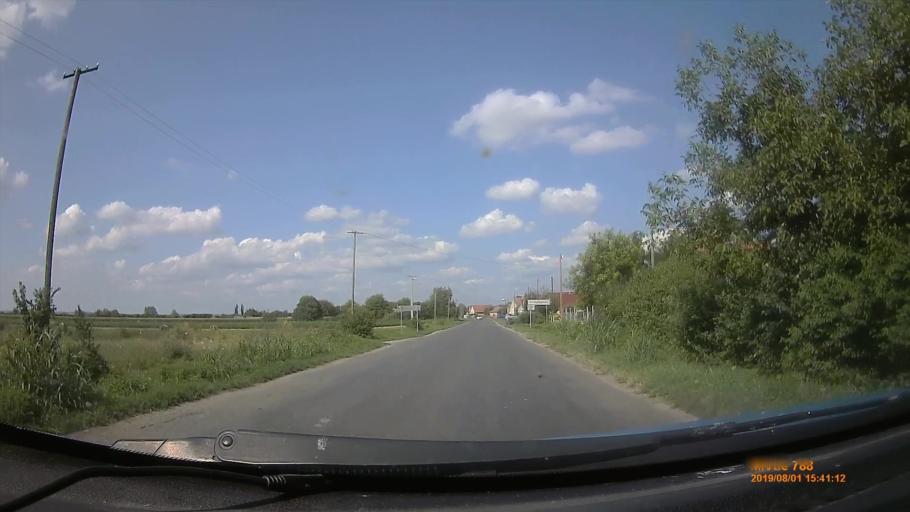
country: HU
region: Baranya
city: Szentlorinc
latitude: 45.9885
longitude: 17.9595
